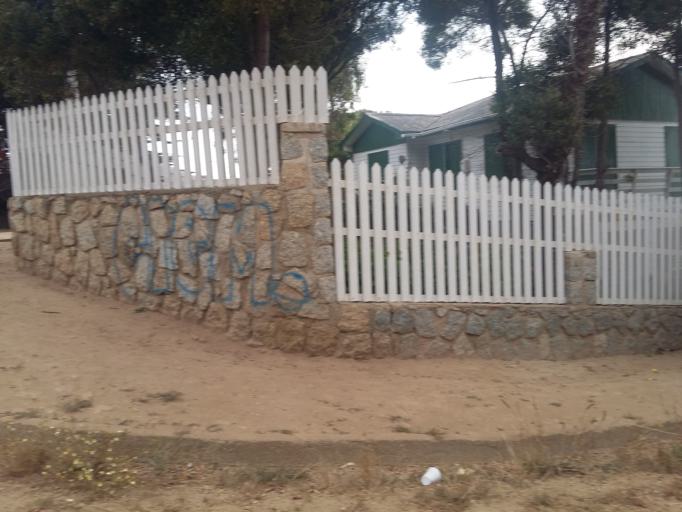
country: CL
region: Valparaiso
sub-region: San Antonio Province
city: El Tabo
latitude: -33.4078
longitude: -71.6976
